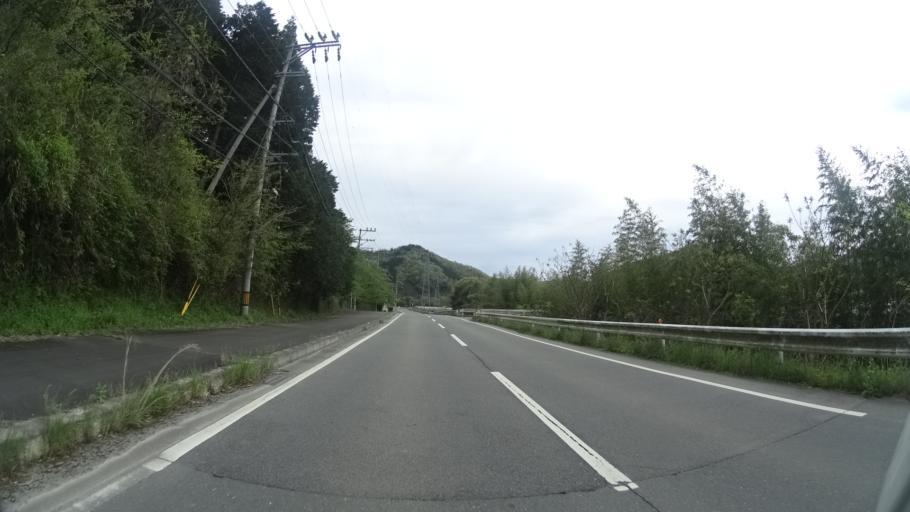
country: JP
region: Kyoto
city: Kameoka
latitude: 35.1224
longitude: 135.5063
